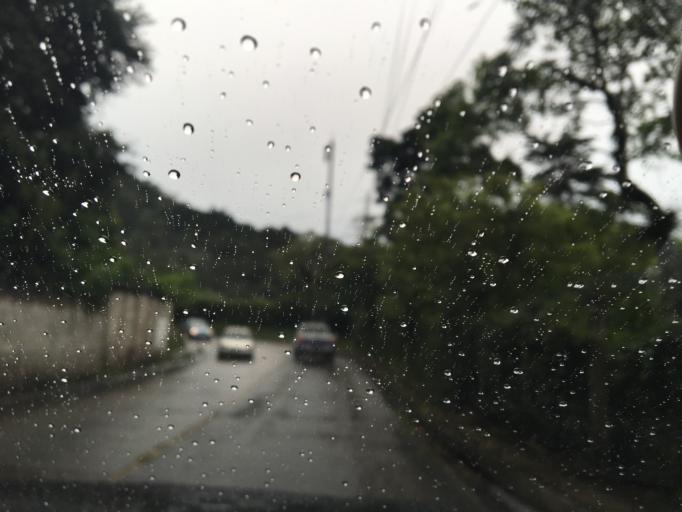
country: GT
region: Guatemala
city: Santa Catarina Pinula
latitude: 14.5552
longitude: -90.4915
